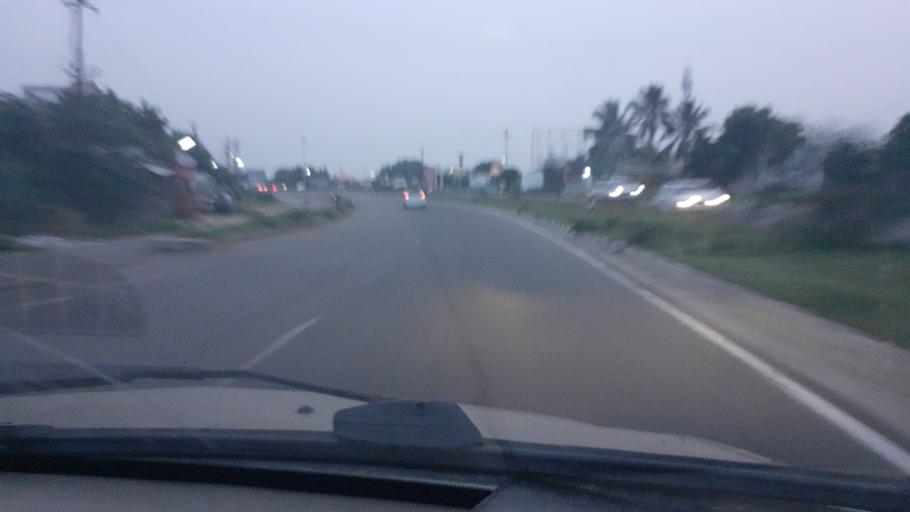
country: IN
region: Tamil Nadu
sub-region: Thoothukkudi
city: Srivaikuntam
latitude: 8.7115
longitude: 77.8241
